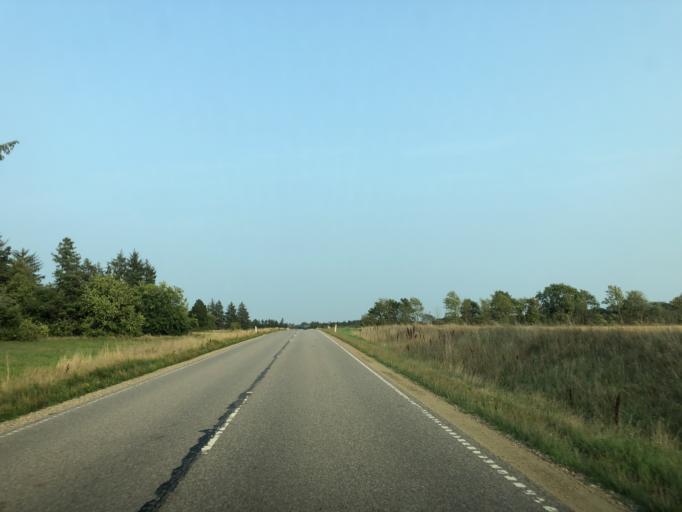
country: DK
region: South Denmark
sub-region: Billund Kommune
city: Grindsted
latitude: 55.8346
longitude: 8.9392
